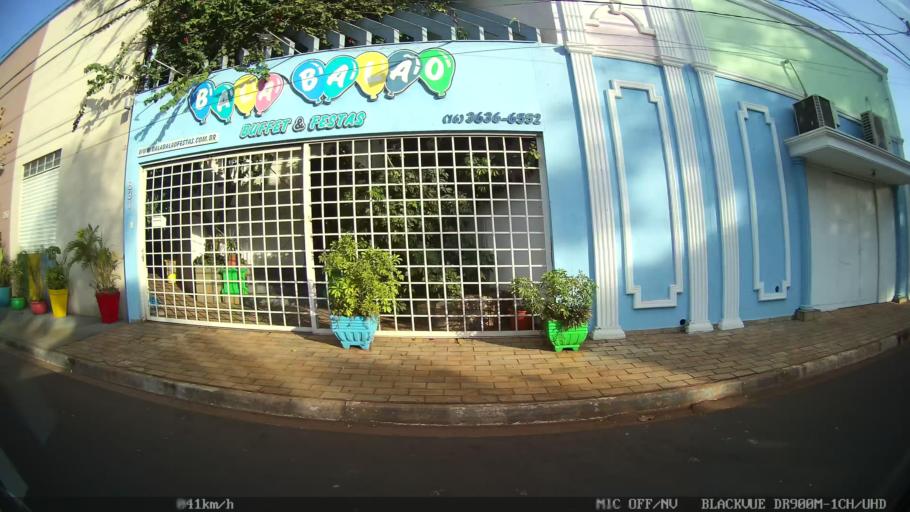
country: BR
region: Sao Paulo
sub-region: Ribeirao Preto
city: Ribeirao Preto
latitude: -21.1648
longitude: -47.8225
